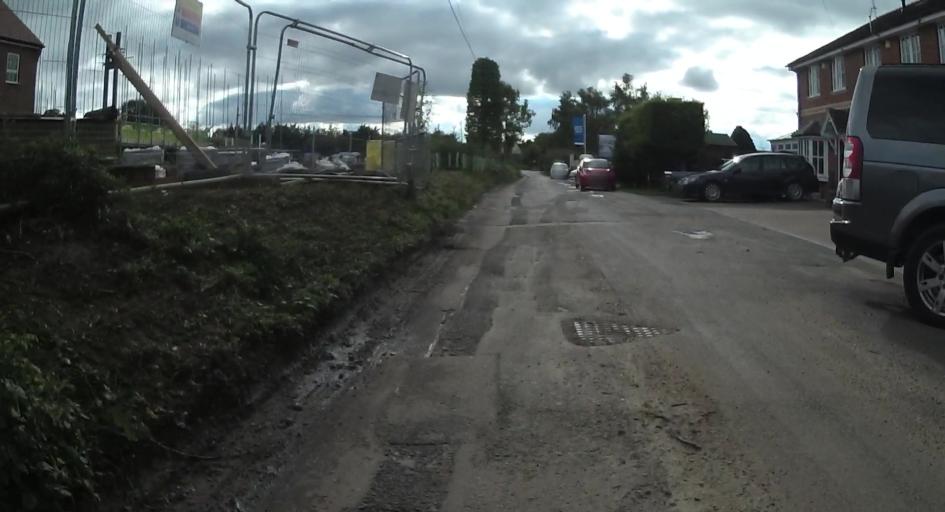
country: GB
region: England
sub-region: Surrey
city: Seale
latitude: 51.2319
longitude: -0.7335
